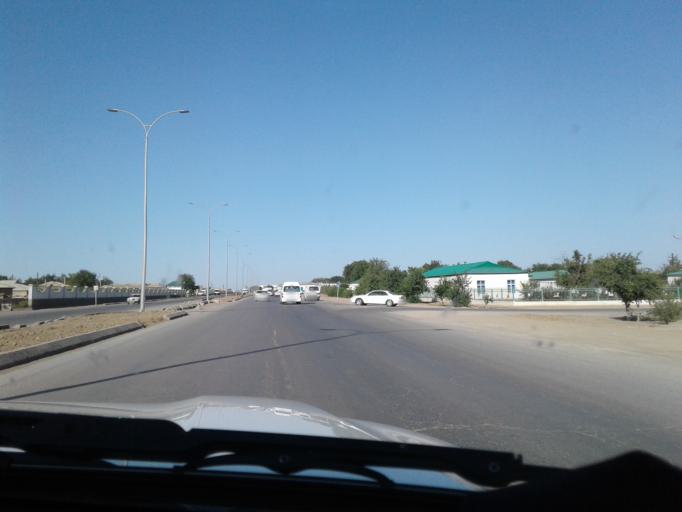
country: TM
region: Ahal
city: Tejen
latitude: 37.3705
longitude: 60.5022
